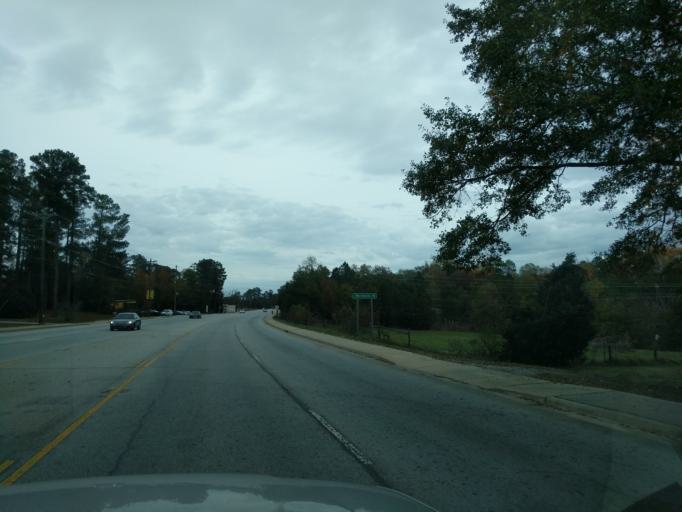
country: US
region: South Carolina
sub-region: Newberry County
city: Newberry
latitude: 34.3092
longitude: -81.6185
